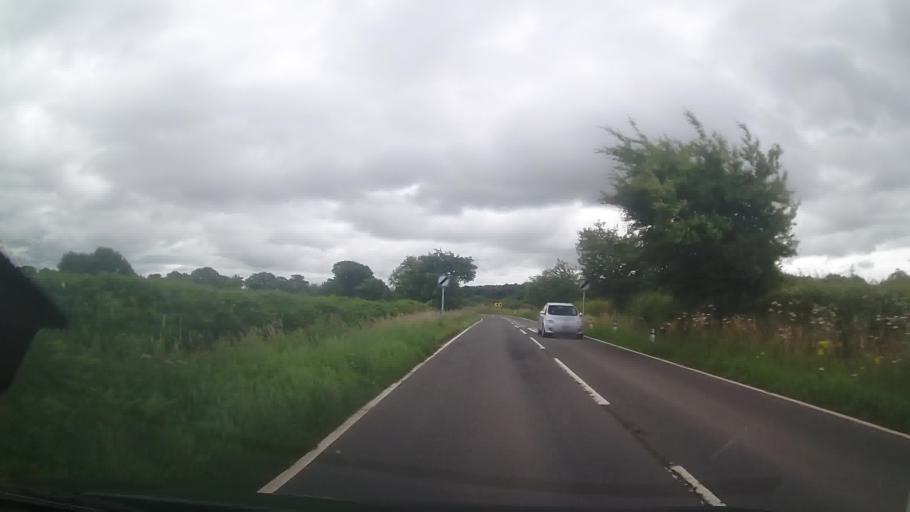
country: GB
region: England
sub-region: Cheshire West and Chester
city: Malpas
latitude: 52.9497
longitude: -2.7585
